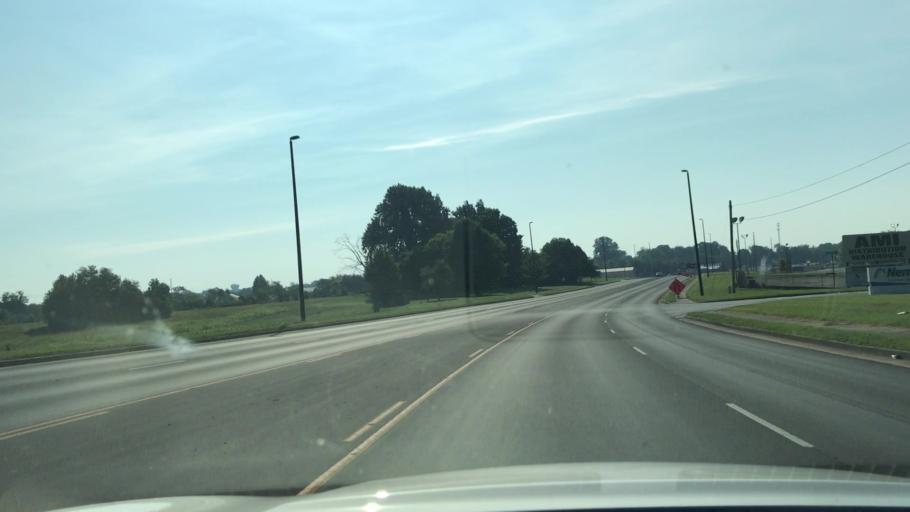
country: US
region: Kentucky
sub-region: Barren County
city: Glasgow
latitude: 37.0099
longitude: -85.9417
